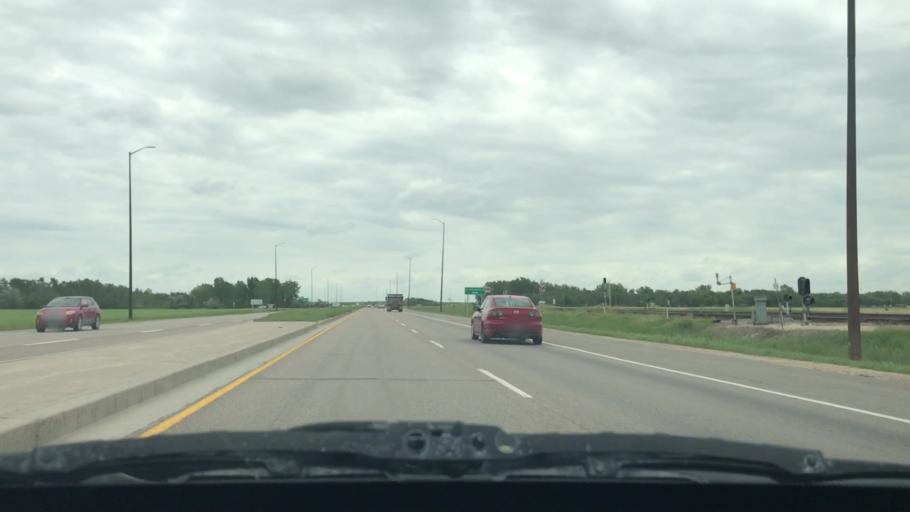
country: CA
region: Manitoba
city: Winnipeg
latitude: 49.8407
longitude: -96.9857
